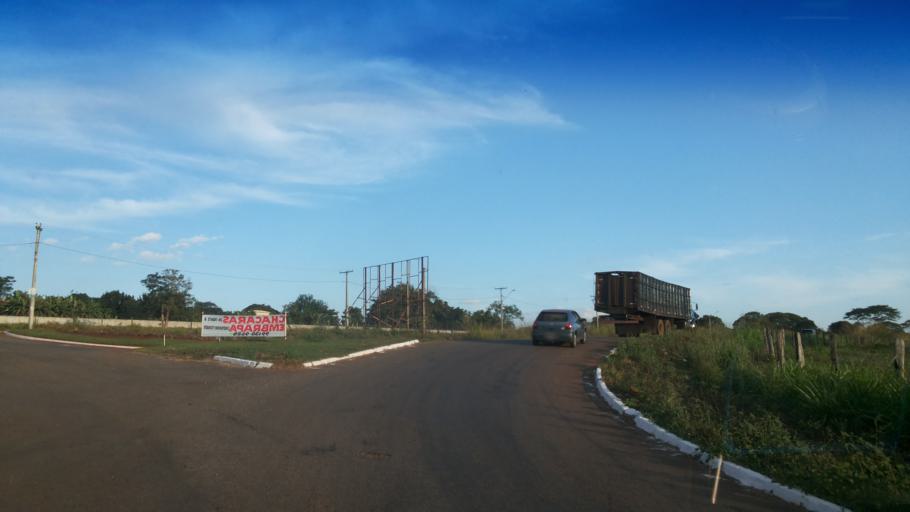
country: BR
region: Goias
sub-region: Neropolis
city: Neropolis
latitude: -16.5161
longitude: -49.2596
